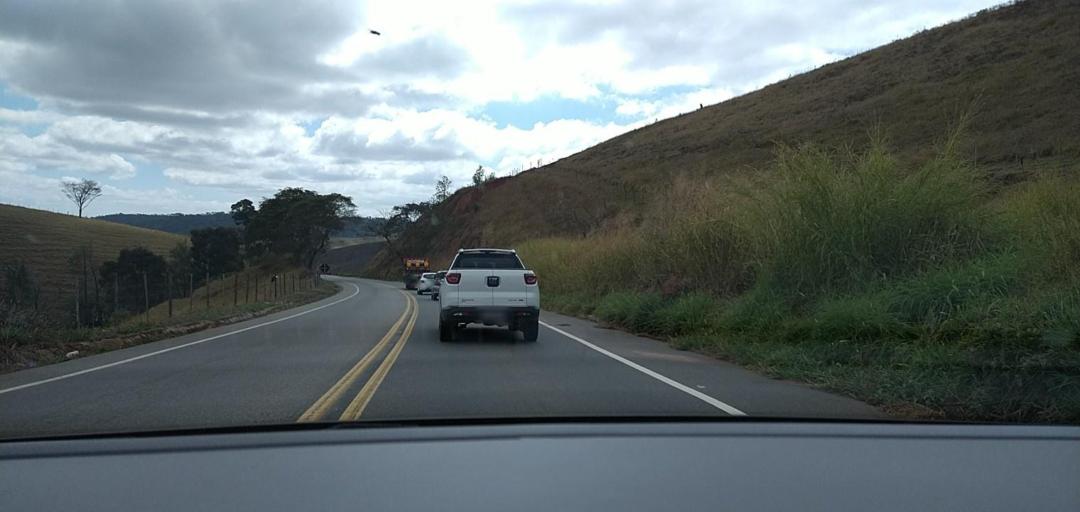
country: BR
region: Minas Gerais
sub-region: Ponte Nova
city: Ponte Nova
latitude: -20.5284
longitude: -42.8948
